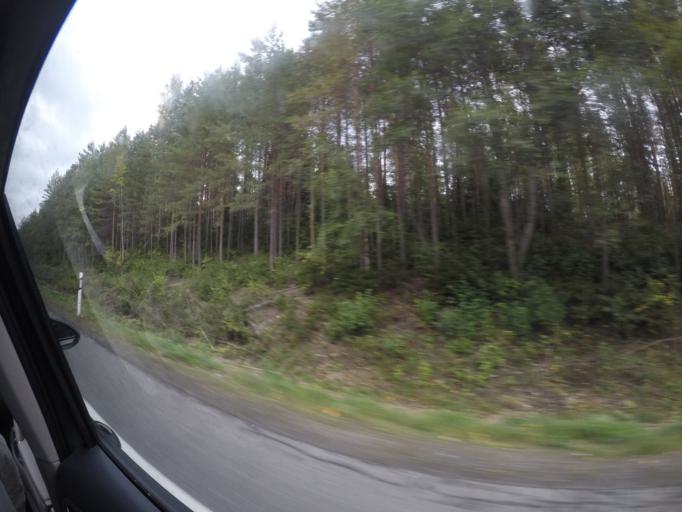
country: FI
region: Haeme
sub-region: Haemeenlinna
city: Parola
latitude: 61.1665
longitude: 24.4110
